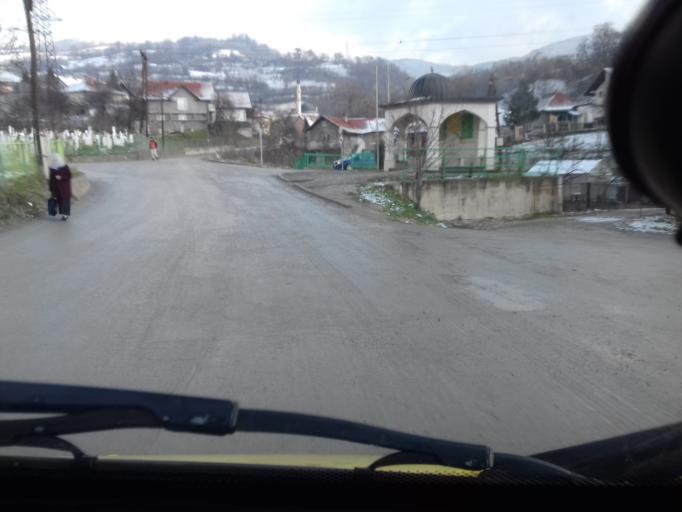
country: BA
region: Federation of Bosnia and Herzegovina
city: Zenica
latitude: 44.2207
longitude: 17.9163
